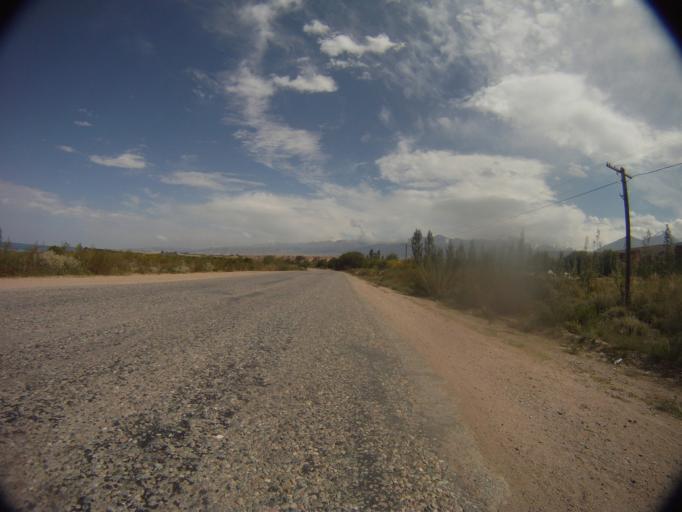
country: KG
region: Ysyk-Koel
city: Kadzhi-Say
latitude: 42.1544
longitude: 77.4958
